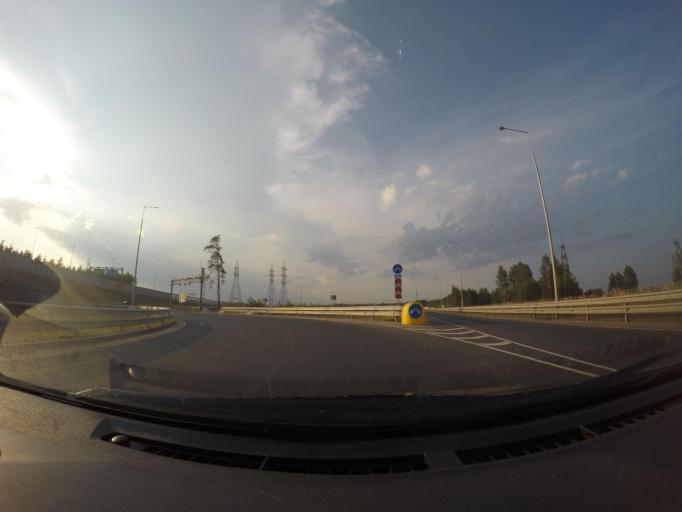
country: RU
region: Moskovskaya
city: Gzhel'
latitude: 55.6336
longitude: 38.3632
